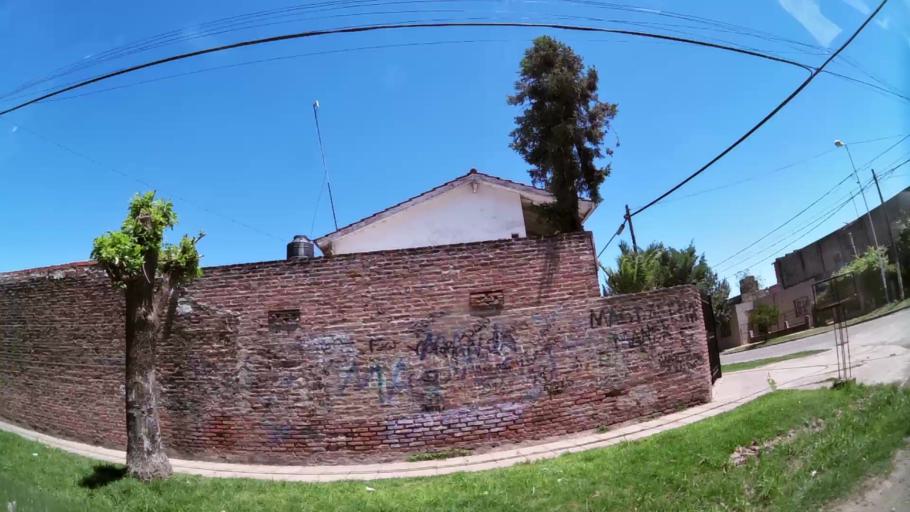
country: AR
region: Buenos Aires
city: Hurlingham
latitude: -34.5038
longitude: -58.7140
